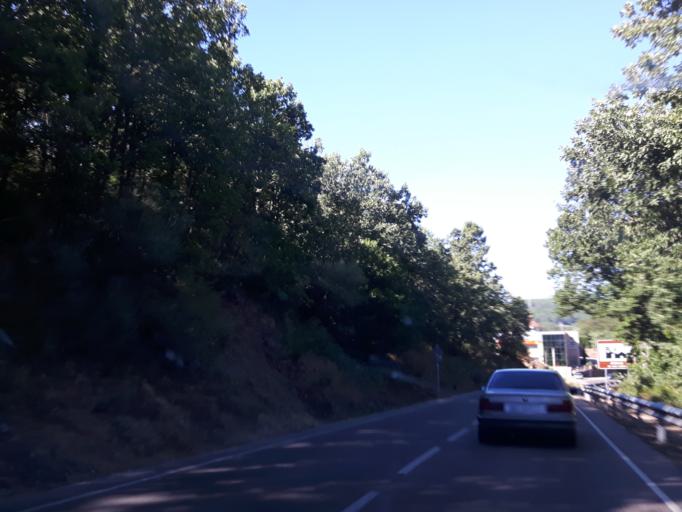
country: ES
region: Castille and Leon
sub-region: Provincia de Avila
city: Arenas de San Pedro
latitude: 40.2169
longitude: -5.0727
